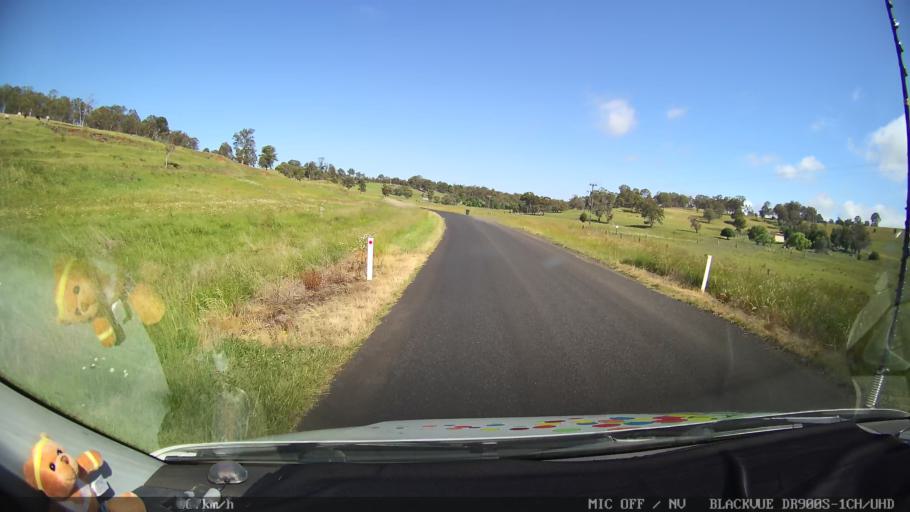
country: AU
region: New South Wales
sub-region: Guyra
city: Guyra
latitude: -30.1182
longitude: 151.6878
